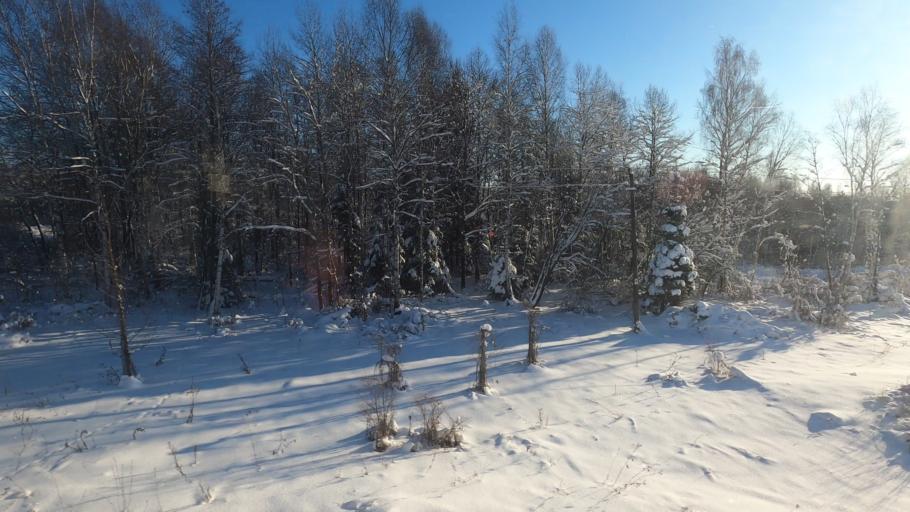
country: RU
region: Moskovskaya
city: Zhukovka
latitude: 56.4694
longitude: 37.5284
